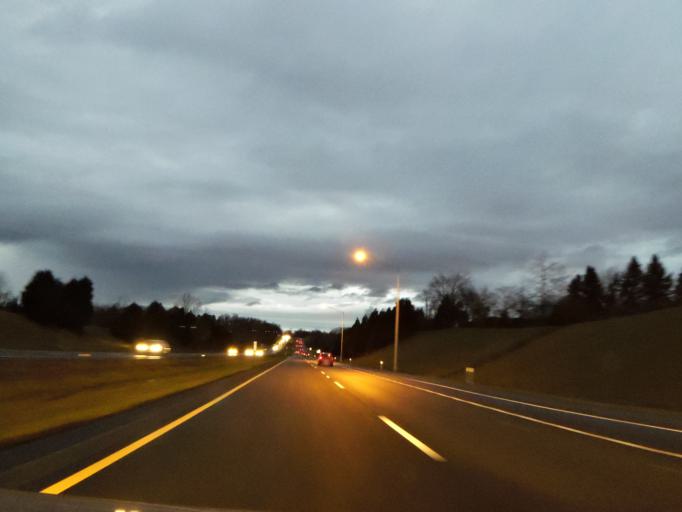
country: US
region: Tennessee
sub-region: Washington County
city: Gray
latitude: 36.4108
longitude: -82.4832
